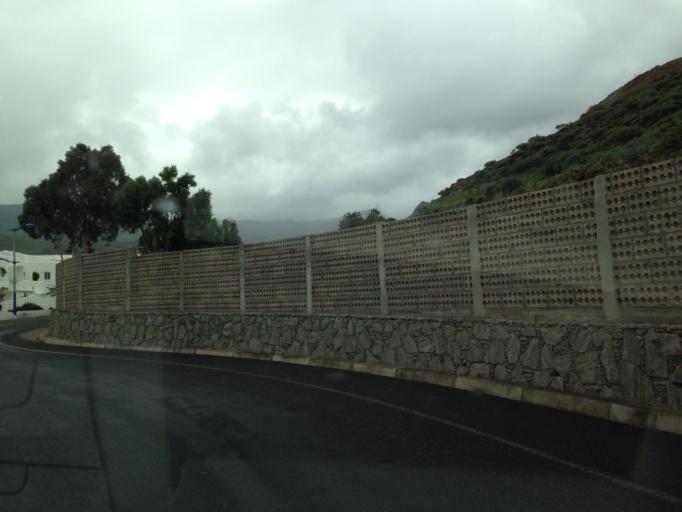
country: ES
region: Canary Islands
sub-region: Provincia de Las Palmas
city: Agaete
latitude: 28.1007
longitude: -15.7076
